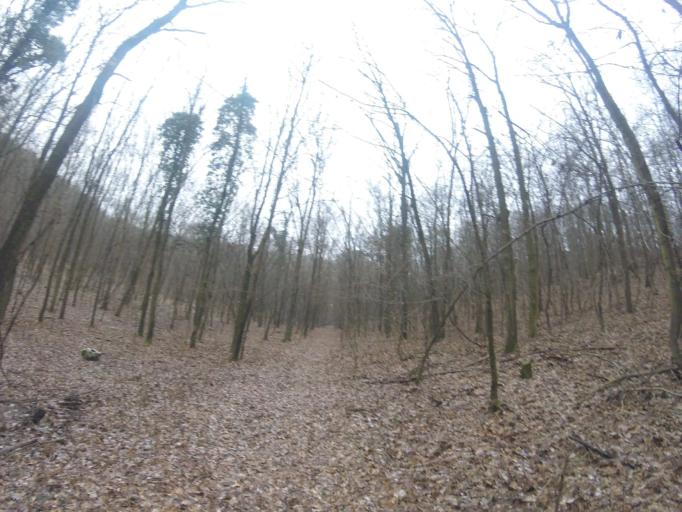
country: HU
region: Fejer
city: Bicske
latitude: 47.4195
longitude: 18.5806
